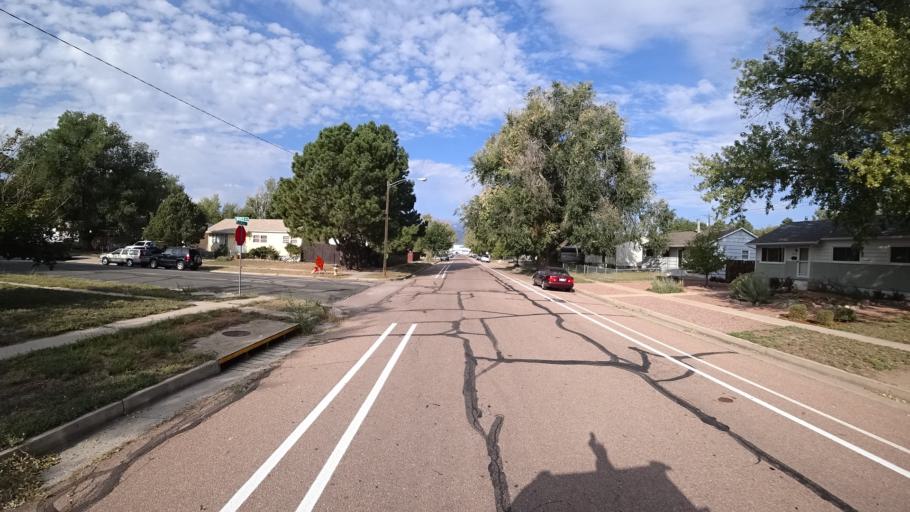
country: US
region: Colorado
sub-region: El Paso County
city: Colorado Springs
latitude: 38.8585
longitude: -104.7694
